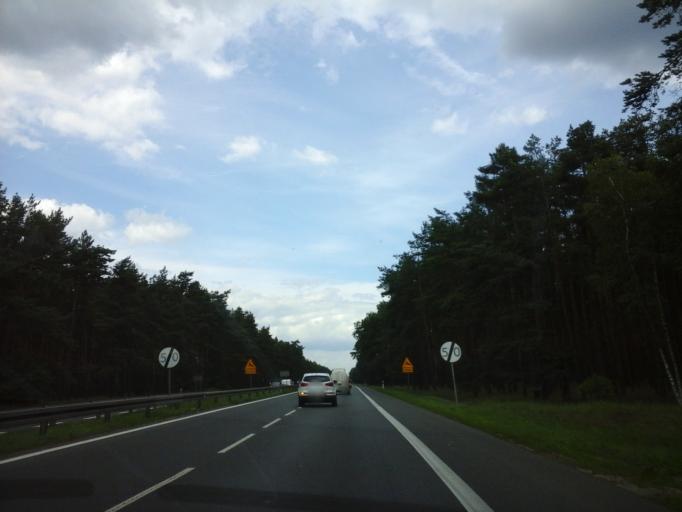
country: PL
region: West Pomeranian Voivodeship
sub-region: Powiat stargardzki
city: Kobylanka
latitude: 53.4281
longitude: 14.7723
